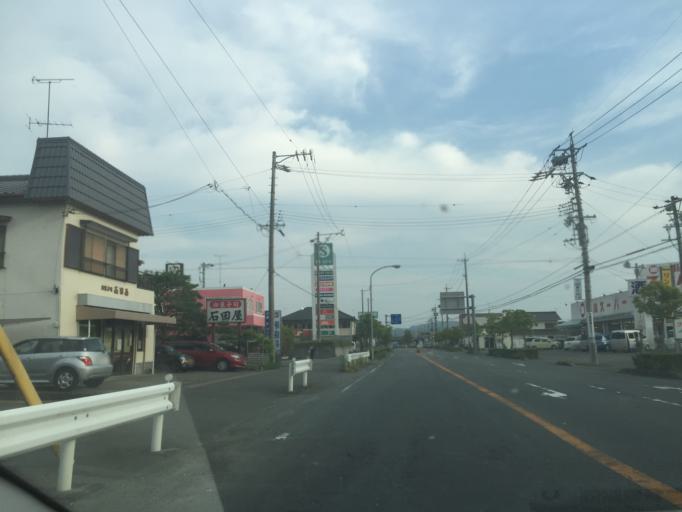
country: JP
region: Shizuoka
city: Kakegawa
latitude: 34.7921
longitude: 138.0128
